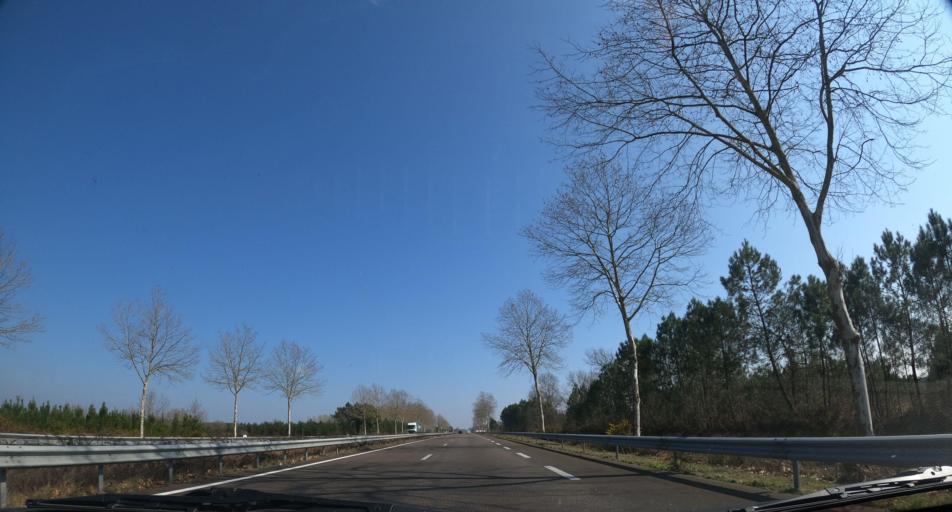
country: FR
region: Aquitaine
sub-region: Departement des Landes
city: Tartas
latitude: 43.8392
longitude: -0.7704
